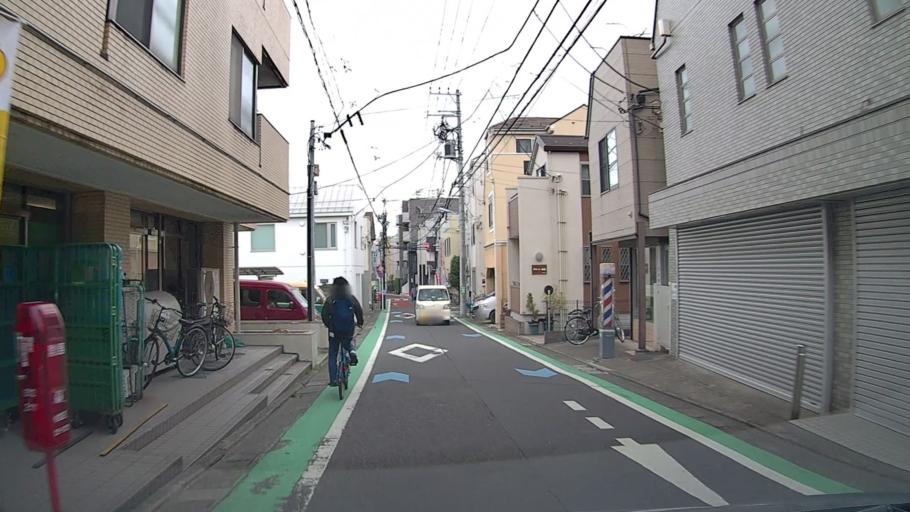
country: JP
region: Tokyo
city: Tokyo
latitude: 35.7021
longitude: 139.6438
